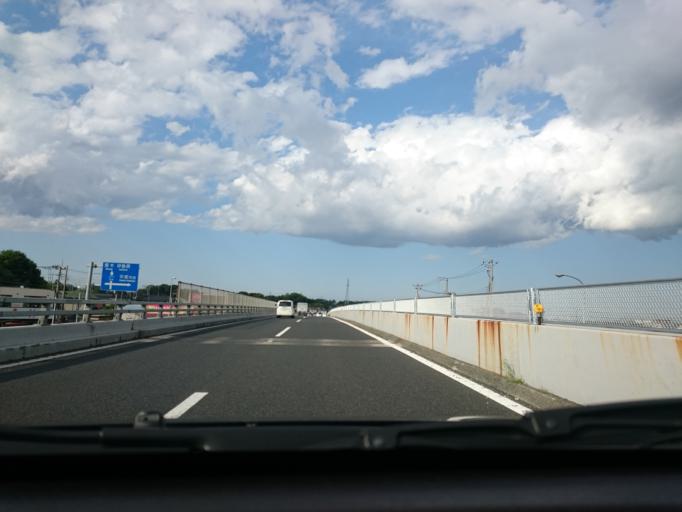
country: JP
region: Kanagawa
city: Isehara
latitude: 35.3691
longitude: 139.3112
